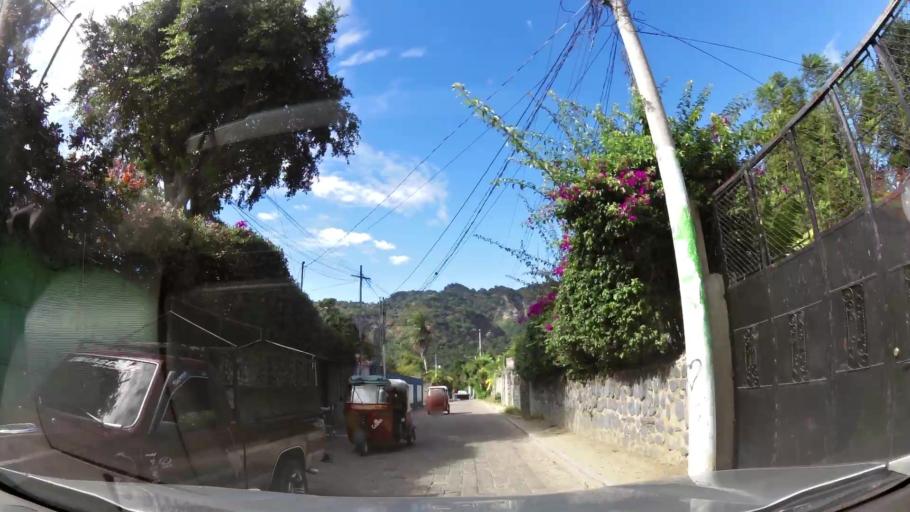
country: GT
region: Solola
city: Panajachel
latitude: 14.7410
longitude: -91.1620
